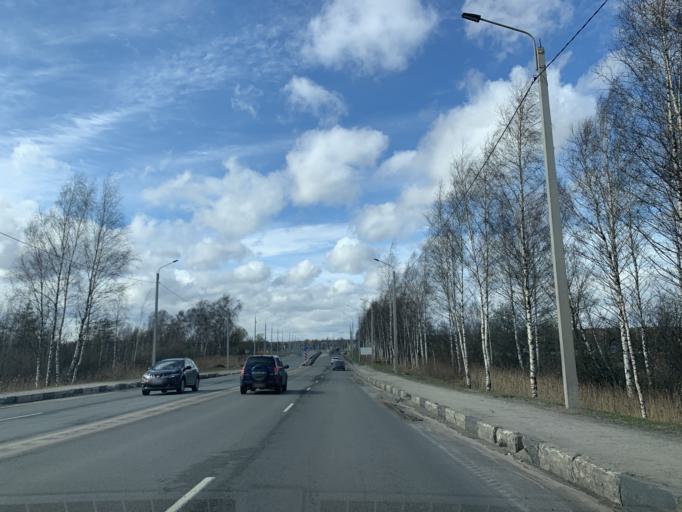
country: RU
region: Jaroslavl
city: Yaroslavl
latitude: 57.6677
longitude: 39.9503
